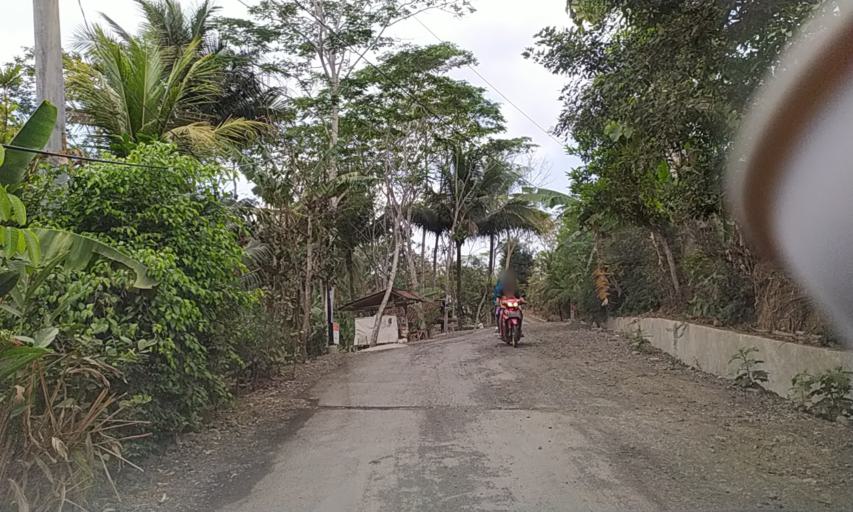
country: ID
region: Central Java
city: Jambuandap
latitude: -7.5643
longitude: 109.0313
